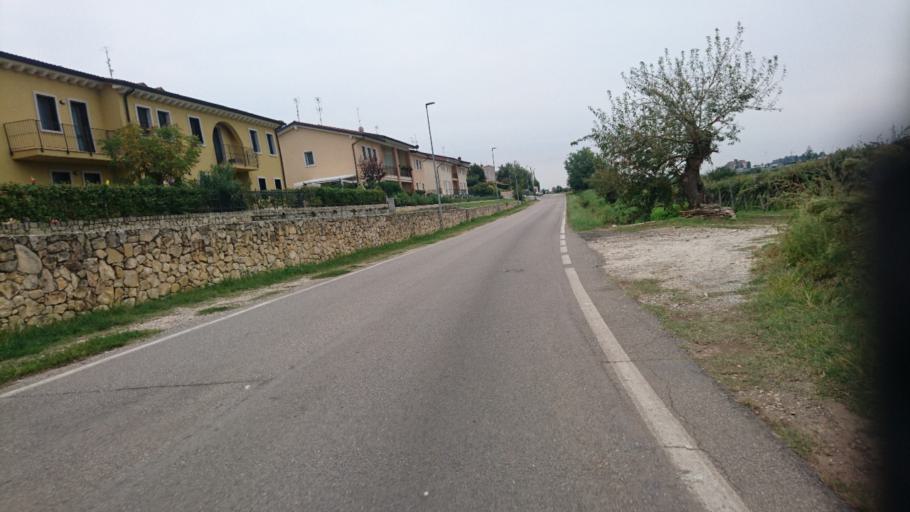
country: IT
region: Veneto
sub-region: Provincia di Verona
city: Soave
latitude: 45.4154
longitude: 11.2544
